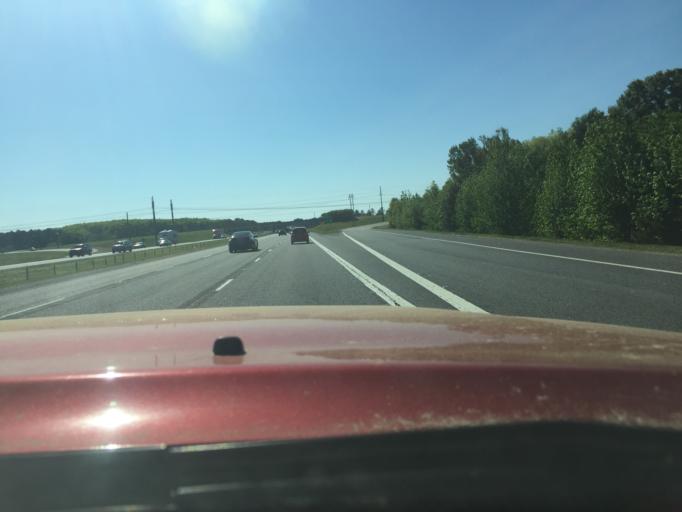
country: US
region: South Carolina
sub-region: Lexington County
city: Cayce
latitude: 33.9290
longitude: -81.0377
